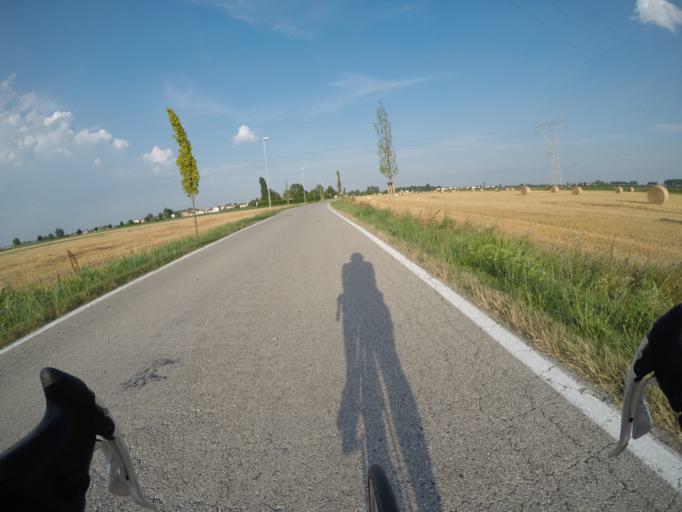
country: IT
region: Veneto
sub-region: Provincia di Rovigo
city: San Bellino
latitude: 45.0279
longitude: 11.5789
